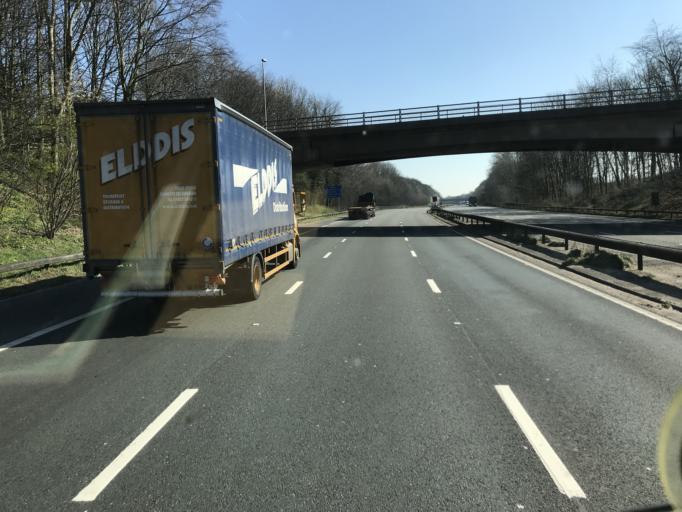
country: GB
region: England
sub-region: Borough of Halton
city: Halton
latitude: 53.3130
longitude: -2.6930
